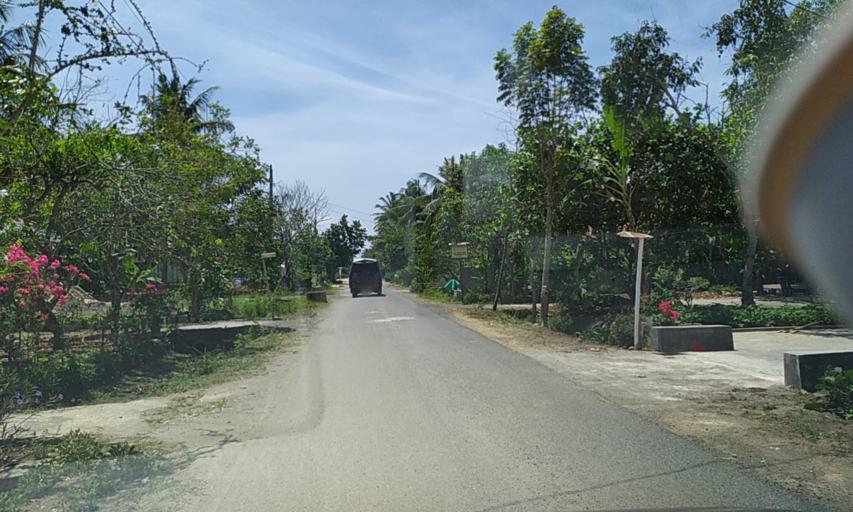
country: ID
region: Central Java
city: Cinyawang
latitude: -7.5603
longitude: 108.7566
